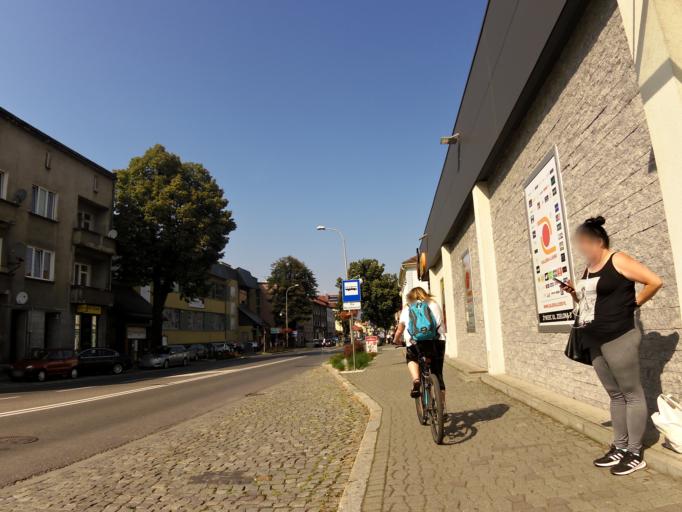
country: PL
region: Silesian Voivodeship
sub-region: Powiat zywiecki
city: Zywiec
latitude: 49.6800
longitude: 19.1877
